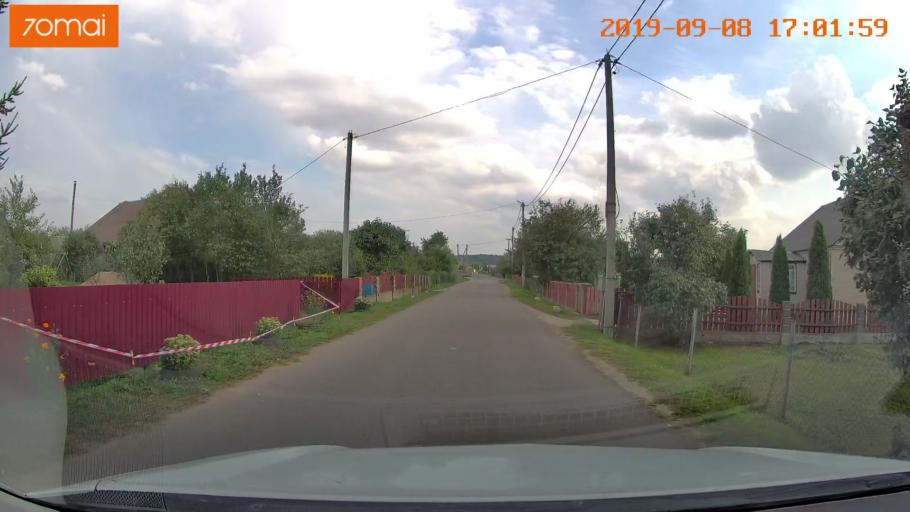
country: BY
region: Grodnenskaya
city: Hrodna
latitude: 53.7061
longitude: 23.9370
